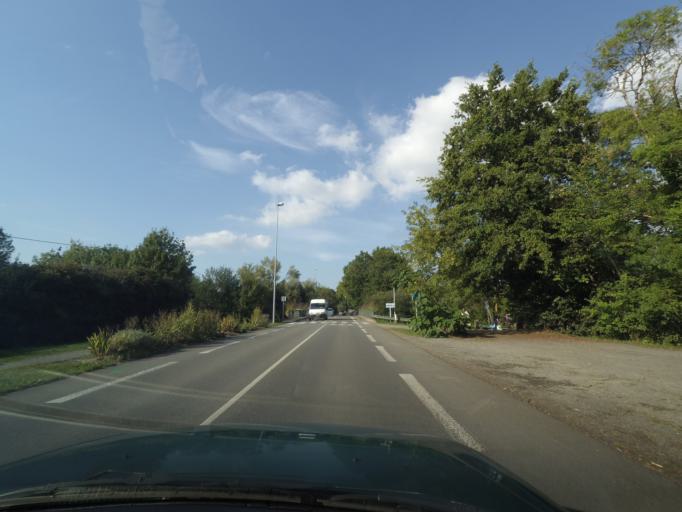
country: FR
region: Pays de la Loire
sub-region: Departement de la Loire-Atlantique
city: Saint-Philbert-de-Grand-Lieu
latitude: 47.0430
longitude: -1.6400
